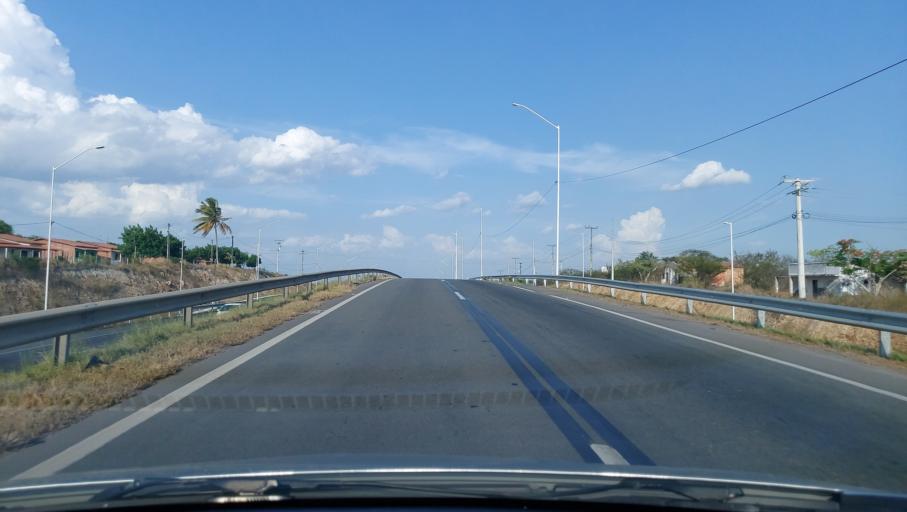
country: BR
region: Bahia
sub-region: Santo Estevao
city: Santo Estevao
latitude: -12.3885
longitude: -39.1420
